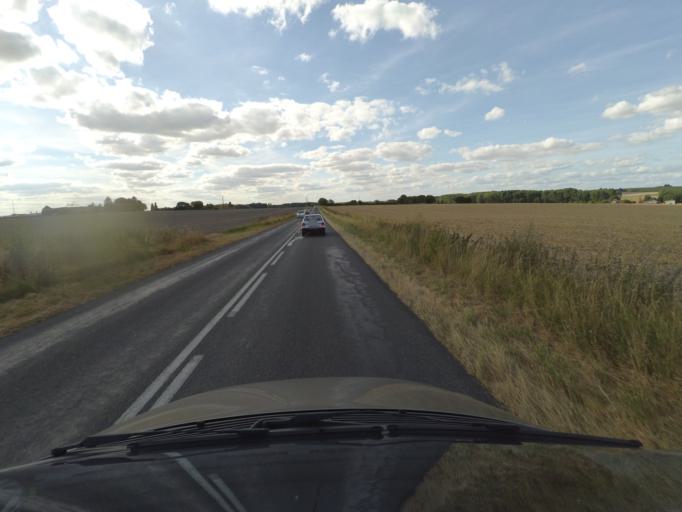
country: FR
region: Poitou-Charentes
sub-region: Departement de la Vienne
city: Saint-Gervais-les-Trois-Clochers
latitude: 46.9620
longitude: 0.3865
